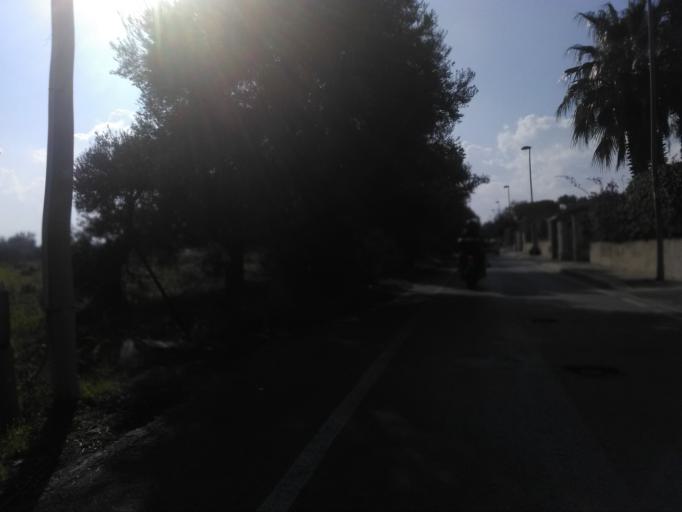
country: IT
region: Apulia
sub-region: Provincia di Bari
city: San Paolo
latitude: 41.1495
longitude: 16.7877
